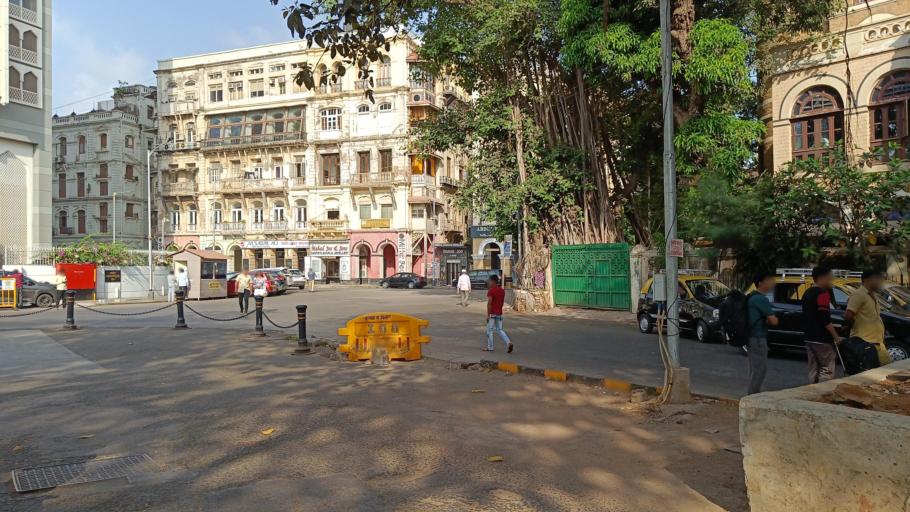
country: IN
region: Maharashtra
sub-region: Raigarh
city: Uran
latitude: 18.9230
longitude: 72.8335
